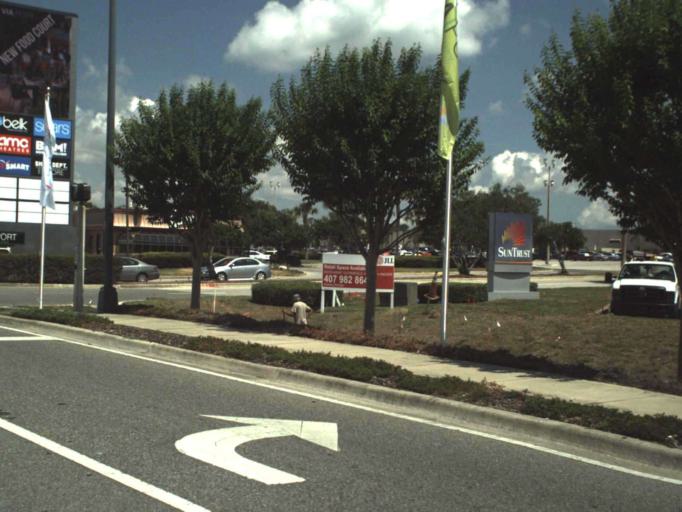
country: US
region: Florida
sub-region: Lake County
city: Silver Lake
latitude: 28.8226
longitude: -81.7844
